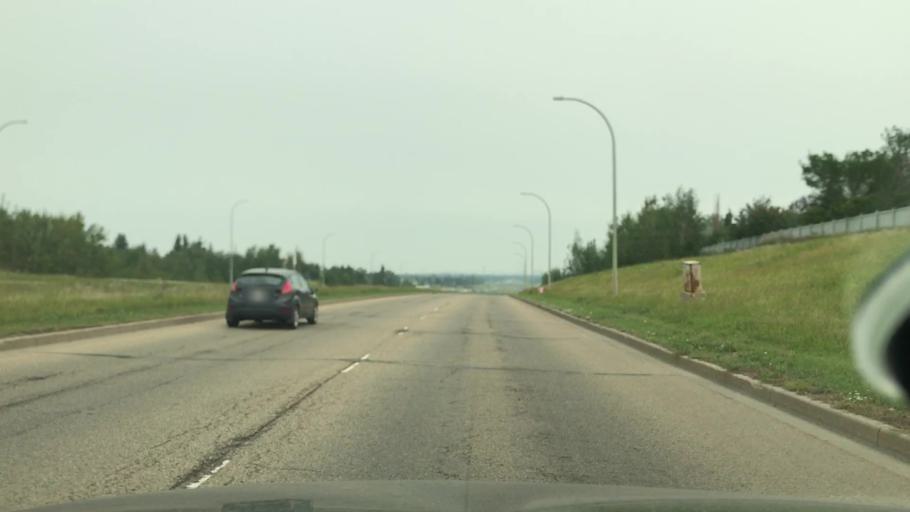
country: CA
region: Alberta
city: Edmonton
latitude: 53.4618
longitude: -113.5868
